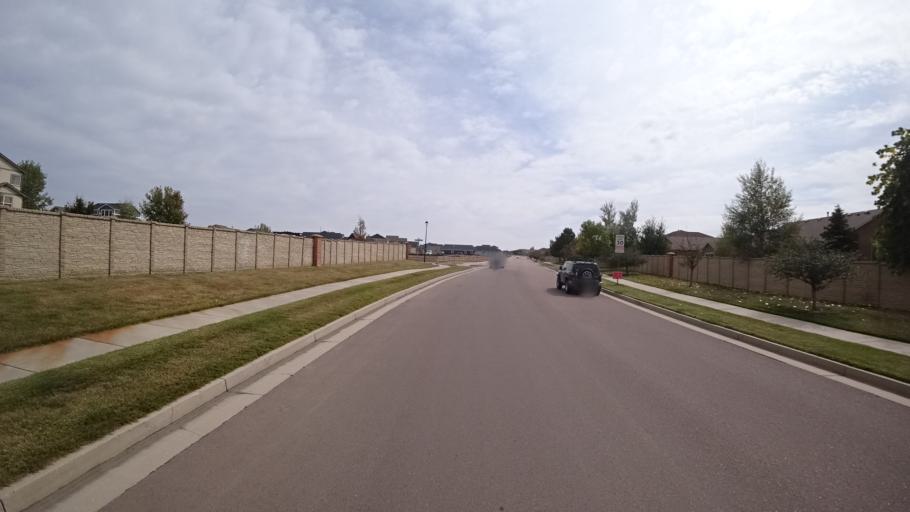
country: US
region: Colorado
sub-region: El Paso County
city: Cimarron Hills
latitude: 38.9240
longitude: -104.6915
